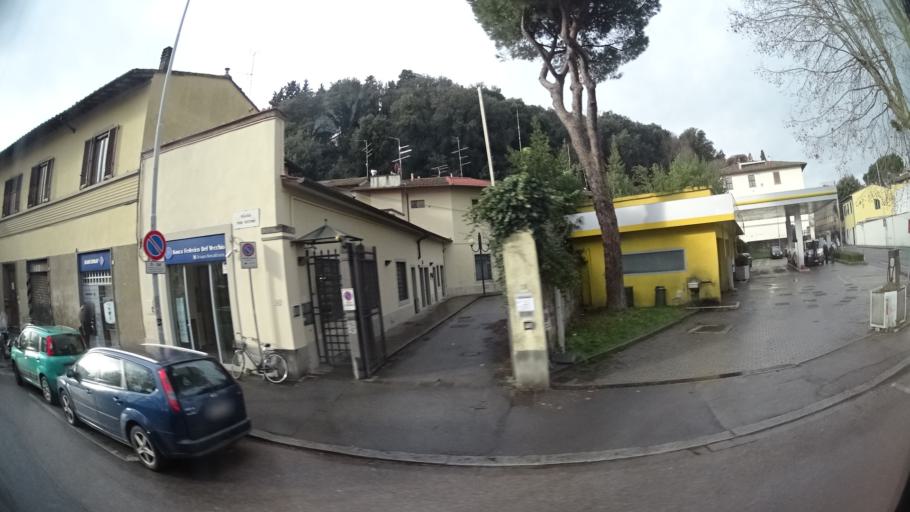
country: IT
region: Tuscany
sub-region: Province of Florence
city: Florence
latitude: 43.7721
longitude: 11.2325
